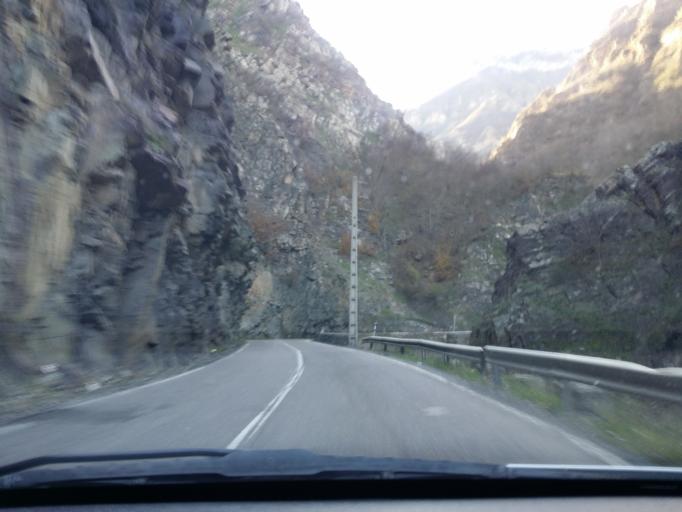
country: IR
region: Mazandaran
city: Chalus
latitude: 36.2815
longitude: 51.2433
